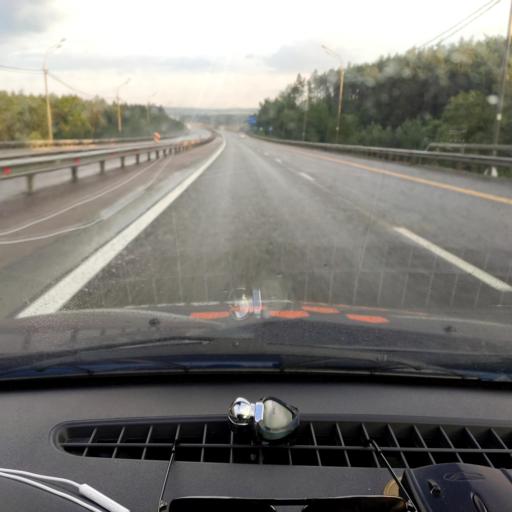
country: RU
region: Lipetsk
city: Zadonsk
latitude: 52.3673
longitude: 38.9237
